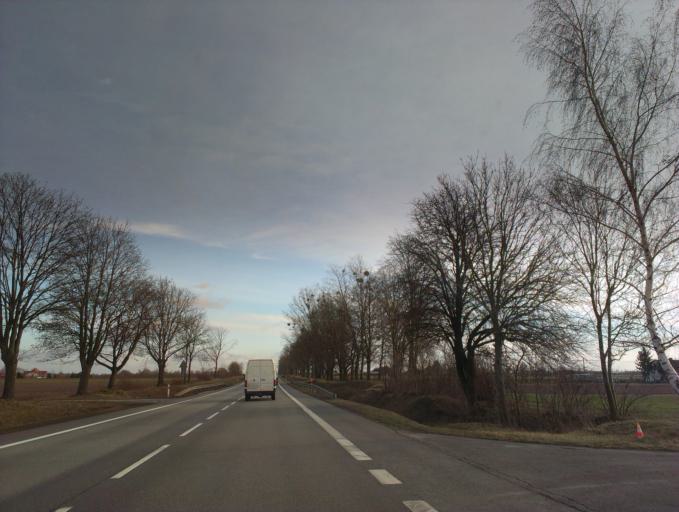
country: PL
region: Kujawsko-Pomorskie
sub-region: Powiat lipnowski
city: Kikol
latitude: 52.9315
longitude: 19.0682
